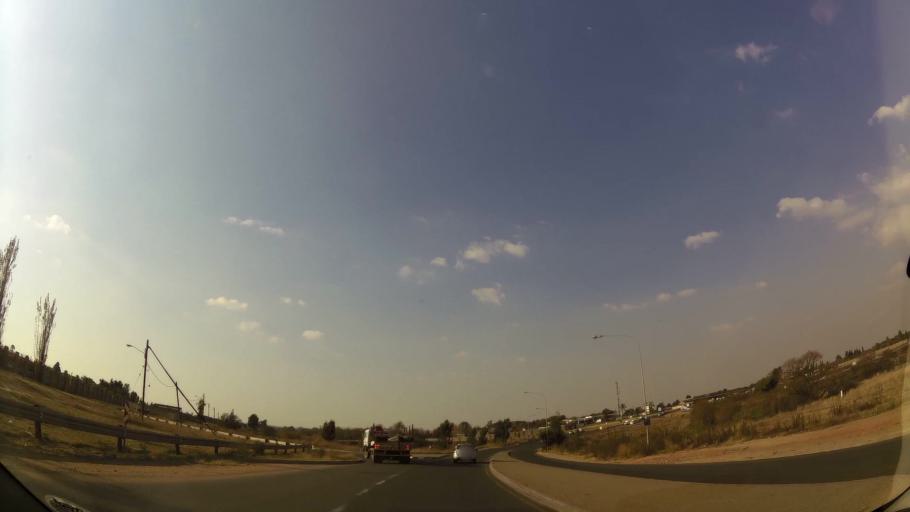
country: ZA
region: Gauteng
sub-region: Ekurhuleni Metropolitan Municipality
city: Tembisa
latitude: -26.0805
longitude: 28.2835
